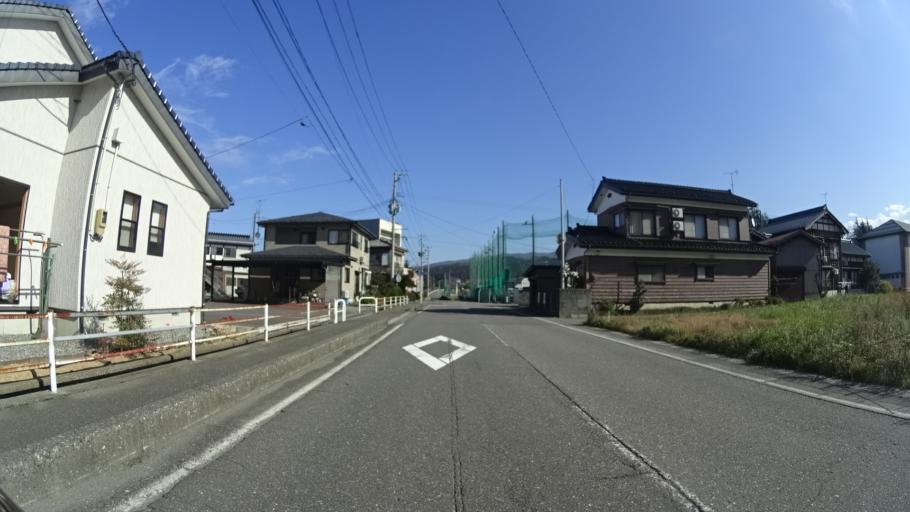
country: JP
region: Niigata
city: Itoigawa
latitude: 37.0421
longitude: 137.8831
